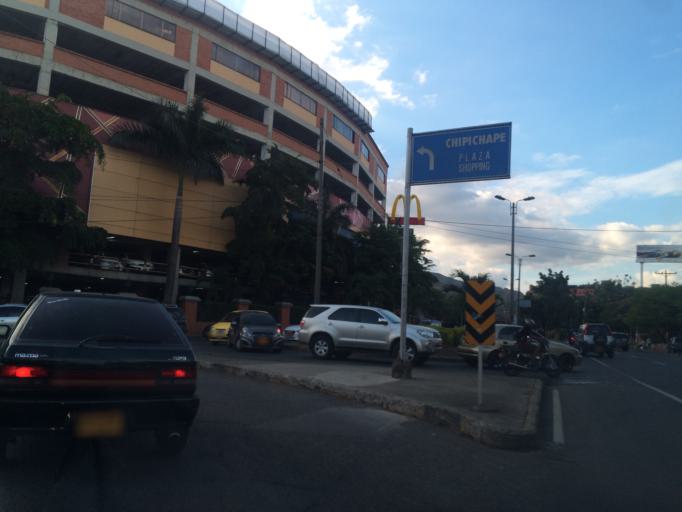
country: CO
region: Valle del Cauca
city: Cali
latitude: 3.4740
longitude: -76.5265
